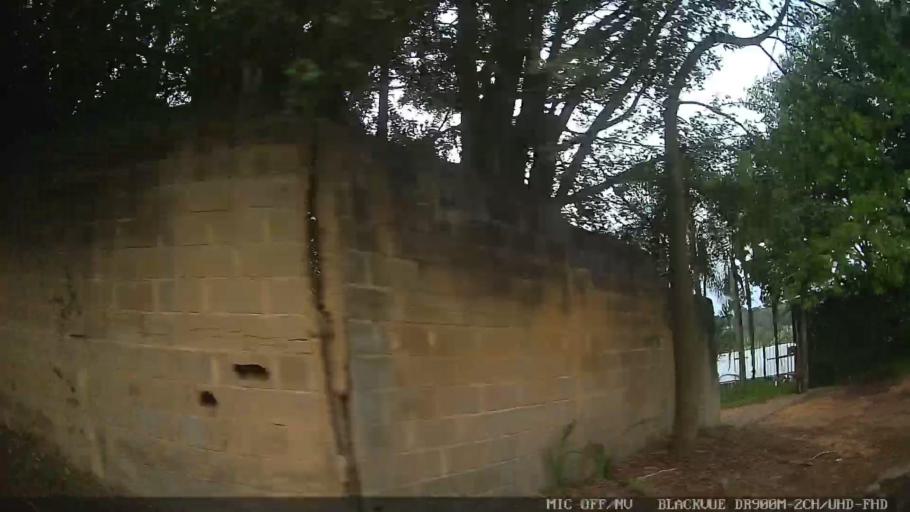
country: BR
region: Sao Paulo
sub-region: Atibaia
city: Atibaia
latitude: -23.1638
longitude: -46.6180
